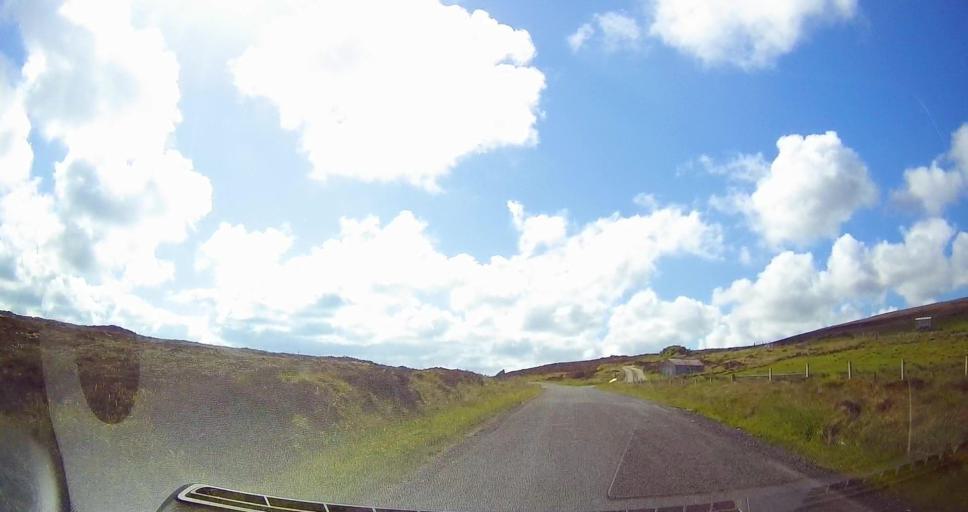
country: GB
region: Scotland
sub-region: Orkney Islands
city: Orkney
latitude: 59.0499
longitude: -3.1169
